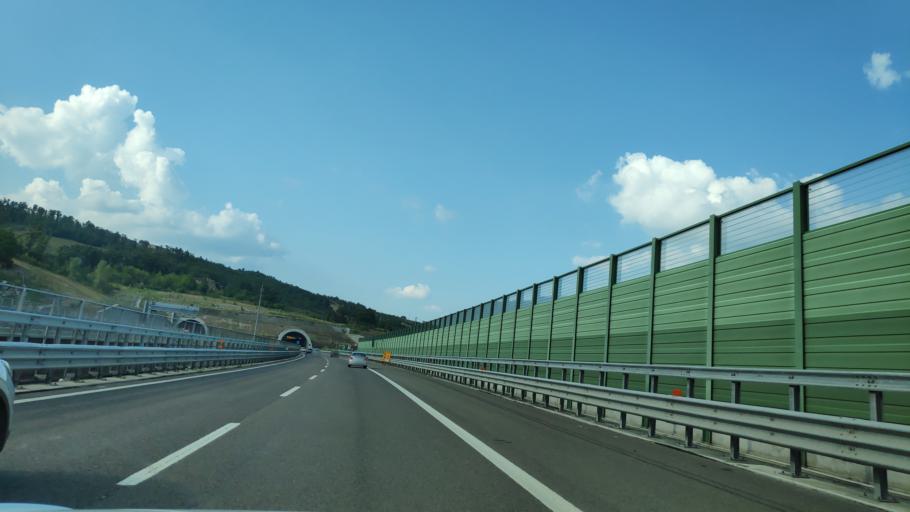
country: IT
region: Emilia-Romagna
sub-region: Provincia di Bologna
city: Castiglione dei Pepoli
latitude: 44.1636
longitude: 11.1974
